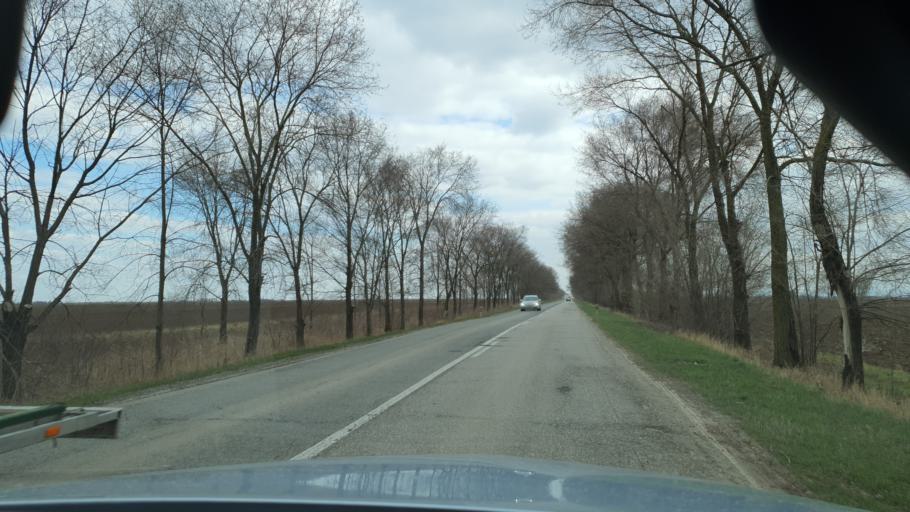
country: RS
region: Autonomna Pokrajina Vojvodina
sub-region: Zapadnobacki Okrug
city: Odzaci
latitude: 45.4475
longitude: 19.3588
